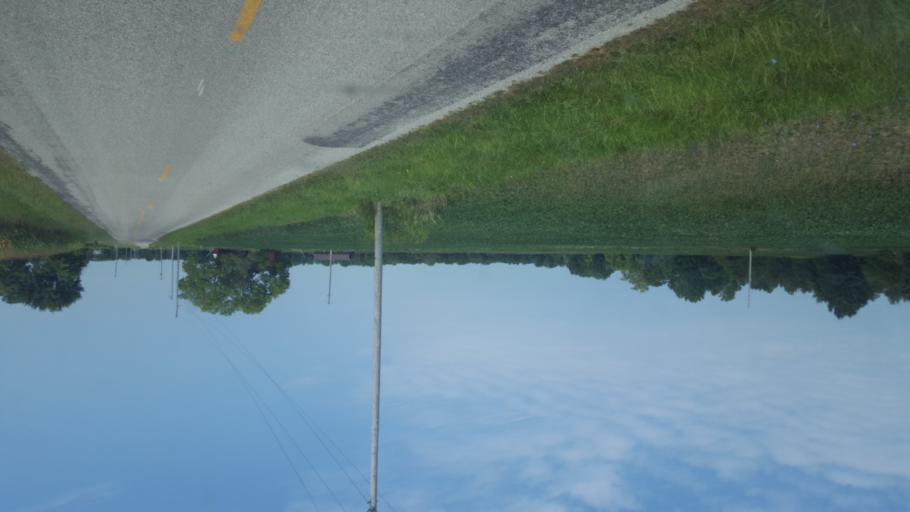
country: US
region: Ohio
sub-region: Delaware County
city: Ashley
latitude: 40.5047
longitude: -83.0280
